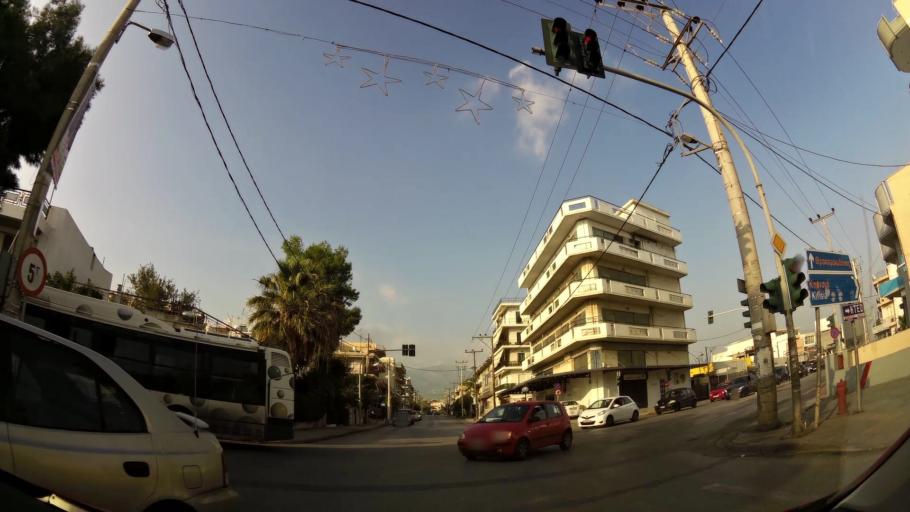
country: GR
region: Attica
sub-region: Nomarchia Anatolikis Attikis
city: Acharnes
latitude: 38.0840
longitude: 23.7452
